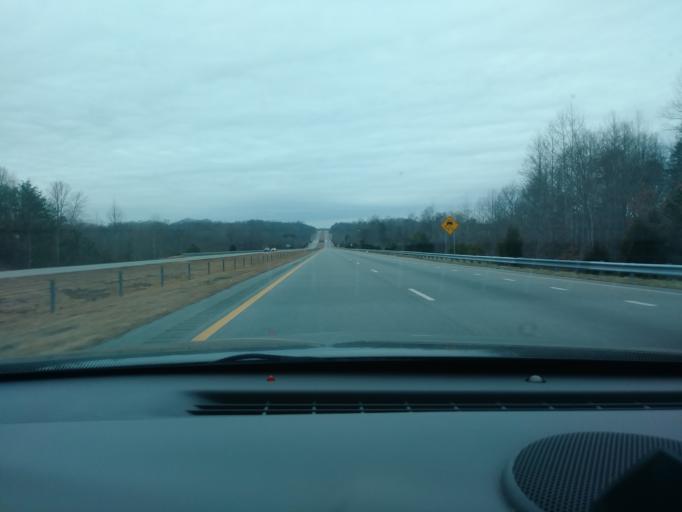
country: US
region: North Carolina
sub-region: Yadkin County
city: Yadkinville
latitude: 36.1191
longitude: -80.7110
